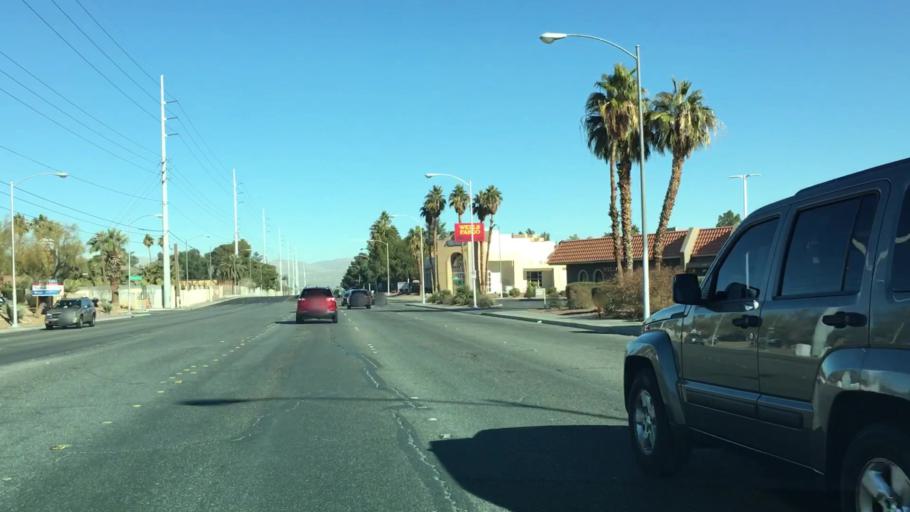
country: US
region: Nevada
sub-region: Clark County
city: Winchester
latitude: 36.1027
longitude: -115.1189
